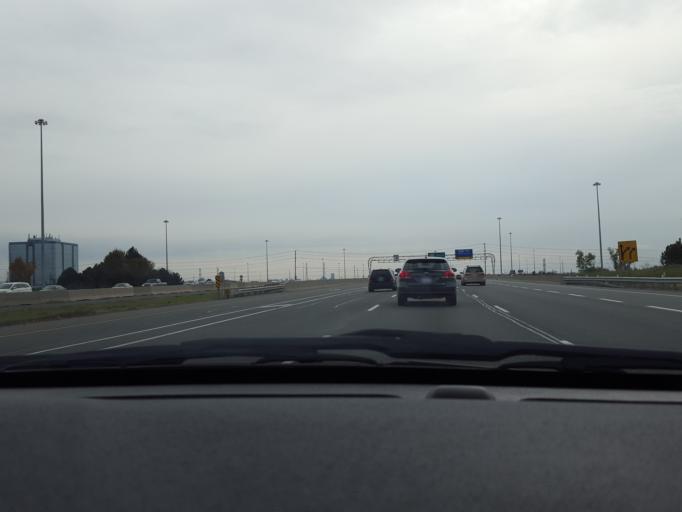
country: CA
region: Ontario
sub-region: York
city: Richmond Hill
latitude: 43.8489
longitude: -79.3718
